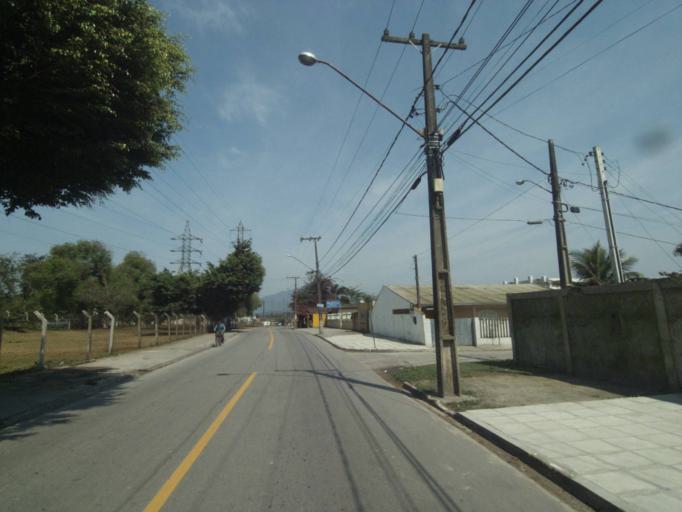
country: BR
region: Parana
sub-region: Paranagua
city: Paranagua
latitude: -25.5452
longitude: -48.5504
